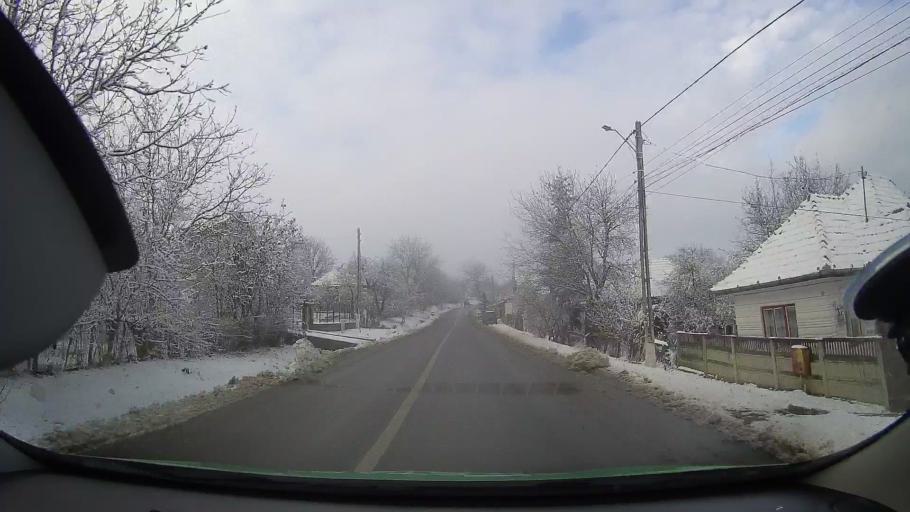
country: RO
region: Mures
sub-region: Comuna Atintis
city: Atintis
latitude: 46.4329
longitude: 24.1003
